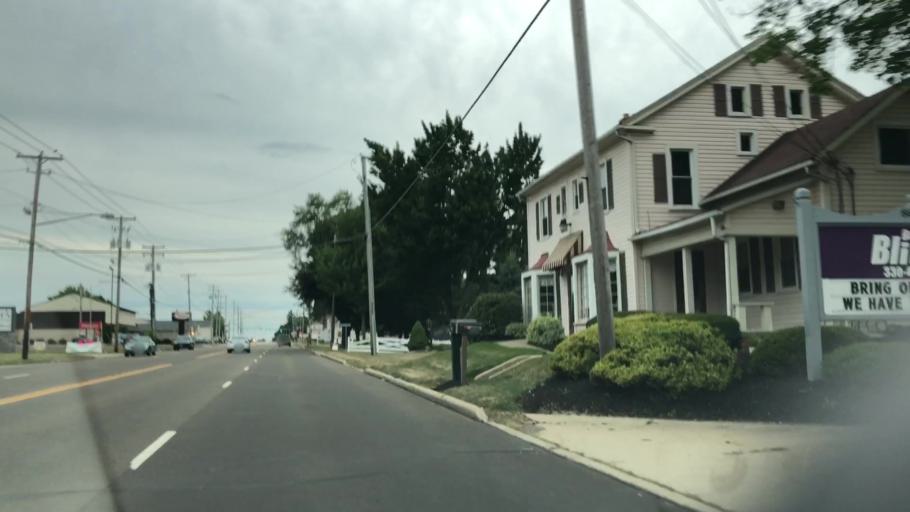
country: US
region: Ohio
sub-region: Stark County
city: Greentown
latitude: 40.9113
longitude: -81.4055
